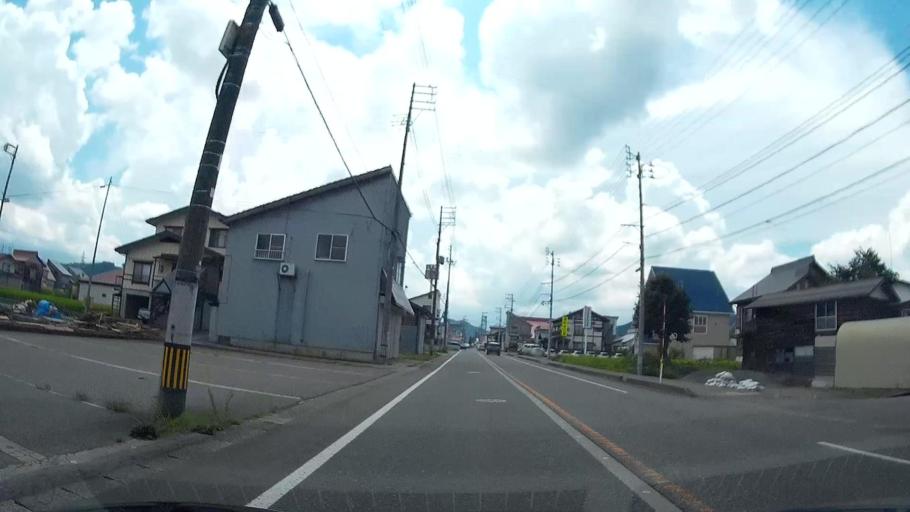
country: JP
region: Niigata
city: Tokamachi
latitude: 37.0210
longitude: 138.6574
